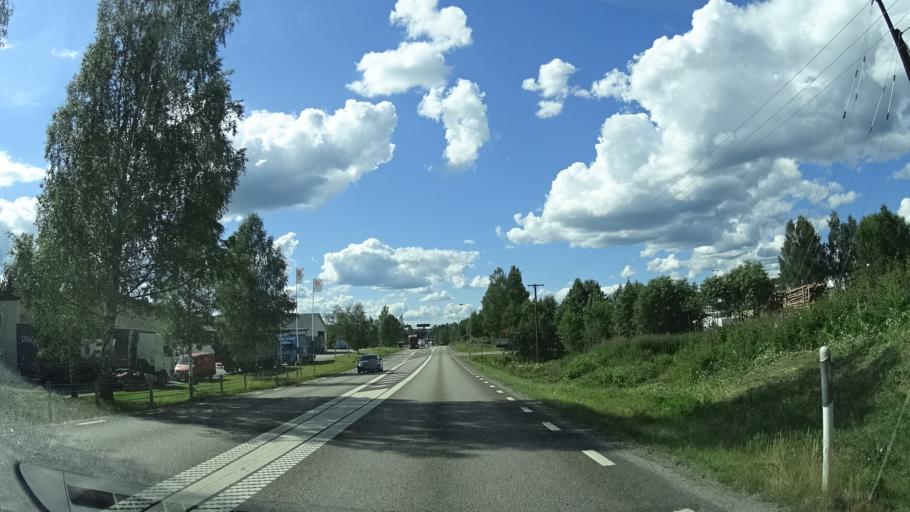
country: SE
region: Vaermland
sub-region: Arjangs Kommun
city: Toecksfors
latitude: 59.5048
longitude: 11.8641
